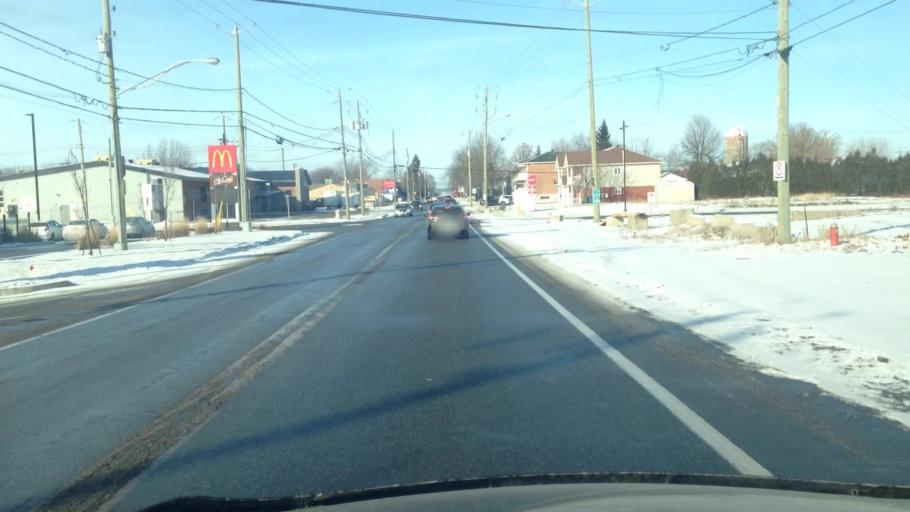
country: CA
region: Quebec
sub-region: Monteregie
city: Beauharnois
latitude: 45.3075
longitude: -73.8603
